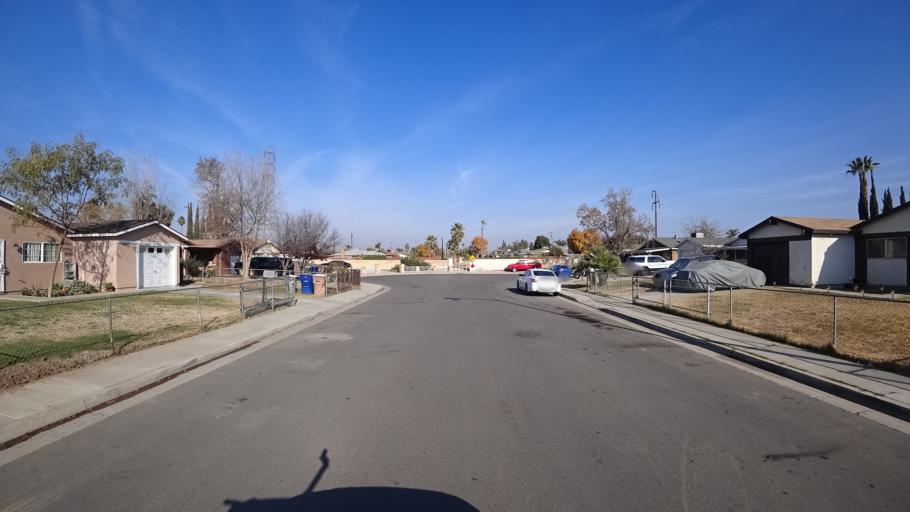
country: US
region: California
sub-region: Kern County
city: Greenfield
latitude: 35.3113
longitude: -119.0147
